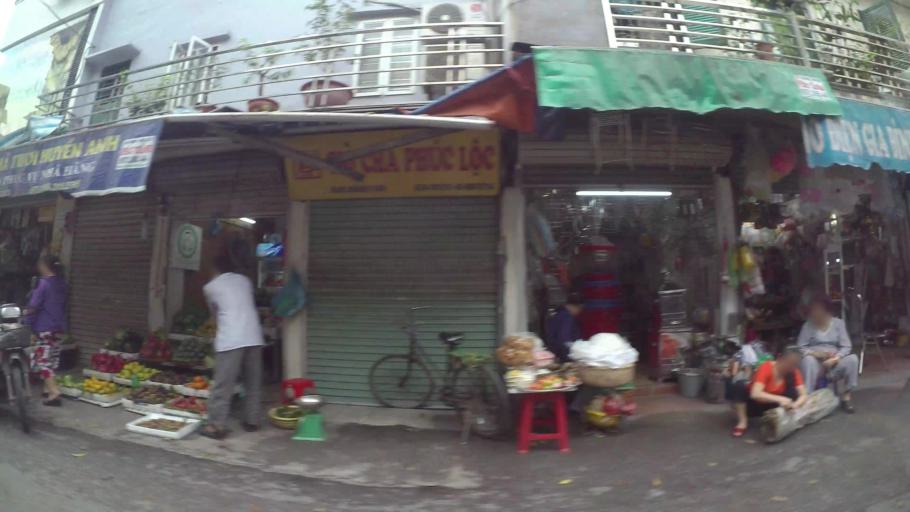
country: VN
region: Ha Noi
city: Hai BaTrung
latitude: 21.0128
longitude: 105.8611
